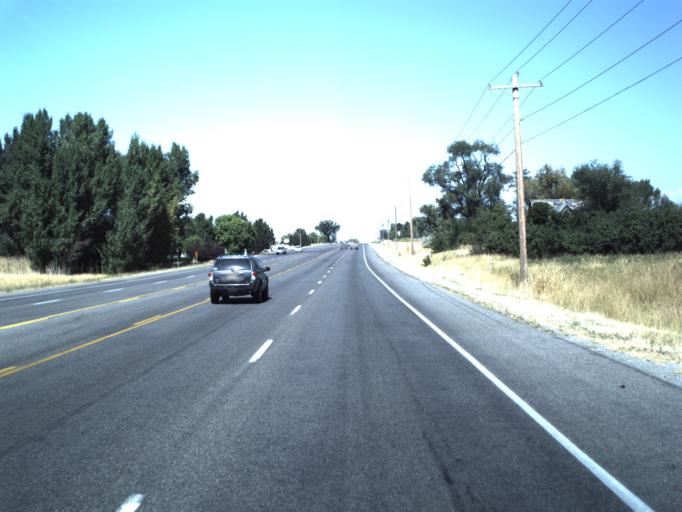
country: US
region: Utah
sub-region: Cache County
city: Richmond
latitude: 41.9362
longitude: -111.8139
